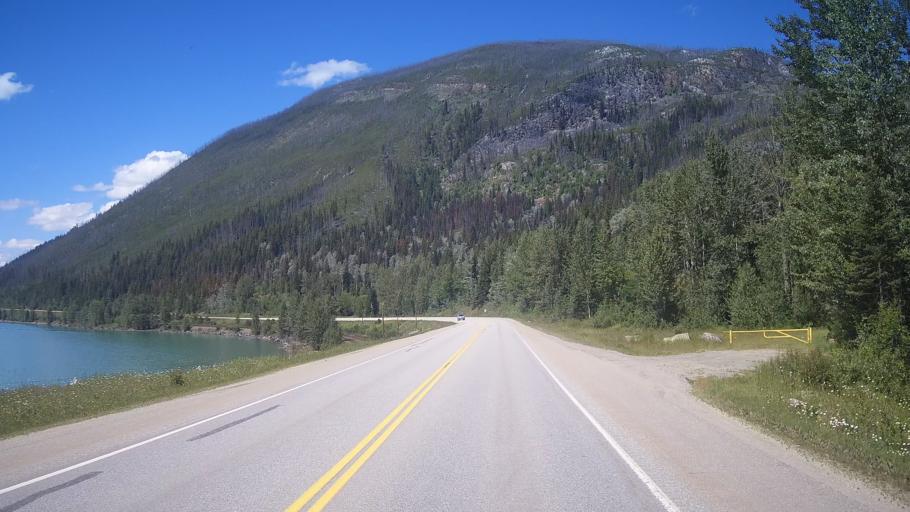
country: CA
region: Alberta
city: Jasper Park Lodge
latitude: 52.9487
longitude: -118.8629
